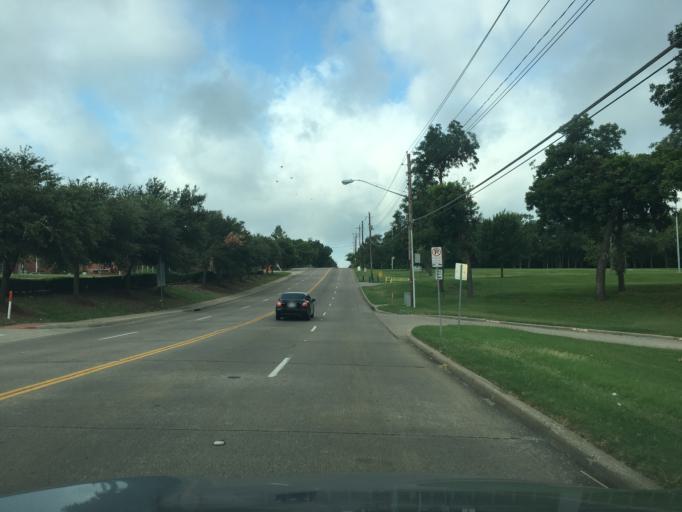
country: US
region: Texas
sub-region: Dallas County
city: University Park
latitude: 32.8781
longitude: -96.7519
